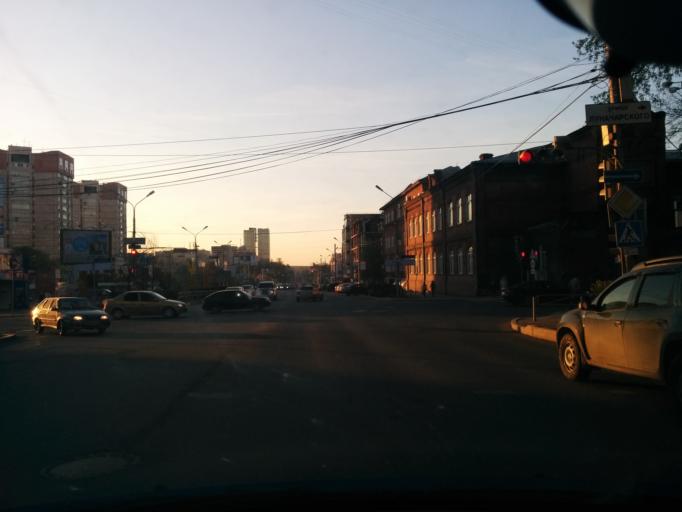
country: RU
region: Perm
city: Perm
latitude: 58.0050
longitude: 56.2297
